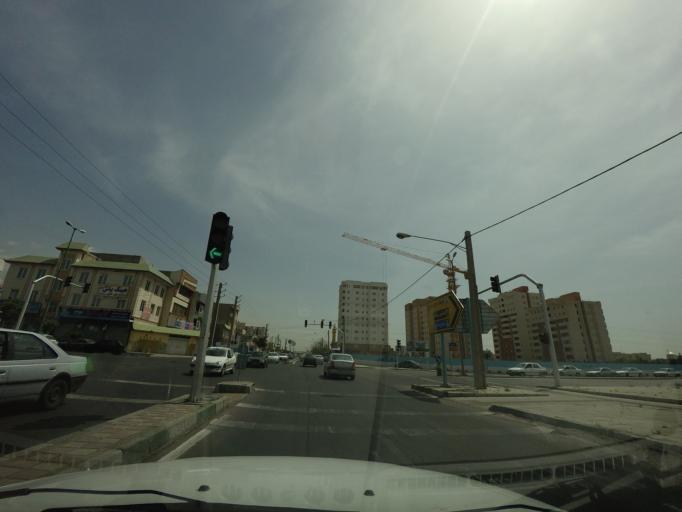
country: IR
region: Tehran
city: Shahr-e Qods
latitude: 35.7457
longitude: 51.2479
